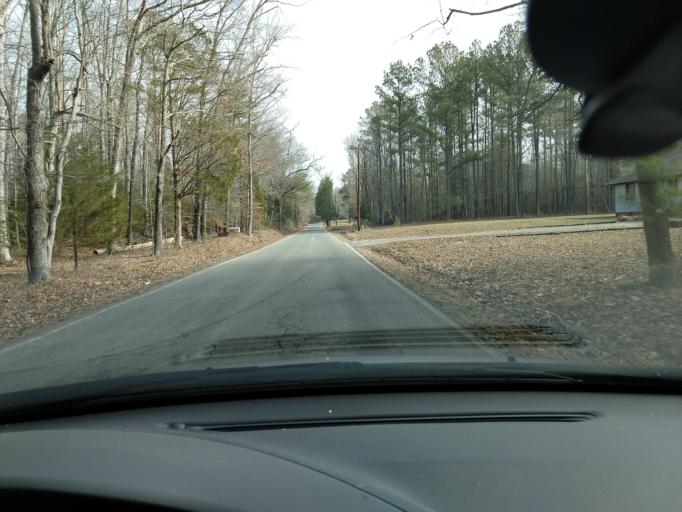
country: US
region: Virginia
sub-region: Henrico County
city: Fort Lee
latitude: 37.4301
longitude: -77.2748
